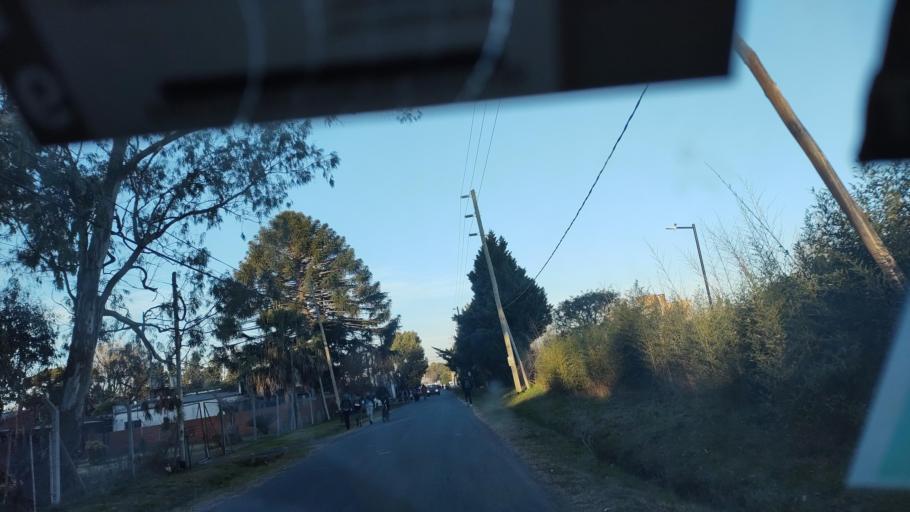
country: AR
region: Buenos Aires
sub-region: Partido de La Plata
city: La Plata
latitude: -34.9048
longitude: -58.0479
